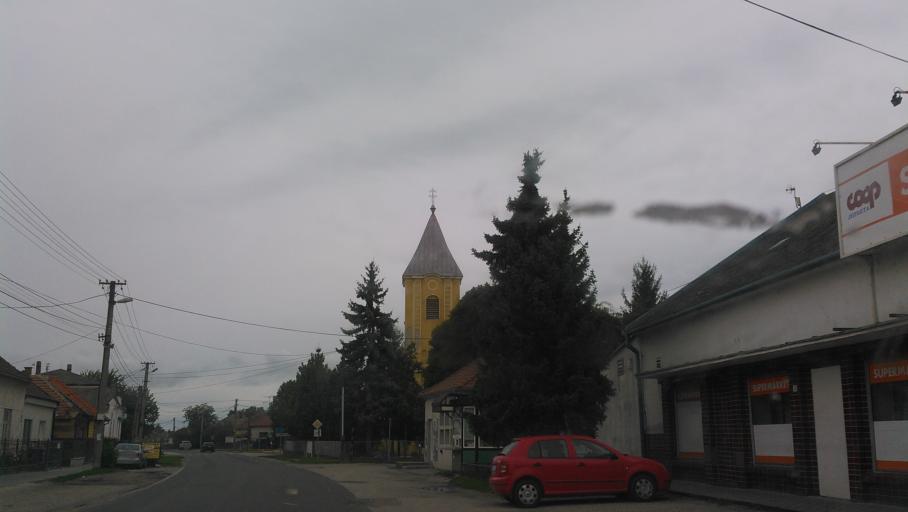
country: SK
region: Trnavsky
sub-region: Okres Dunajska Streda
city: Velky Meder
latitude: 47.8872
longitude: 17.8087
